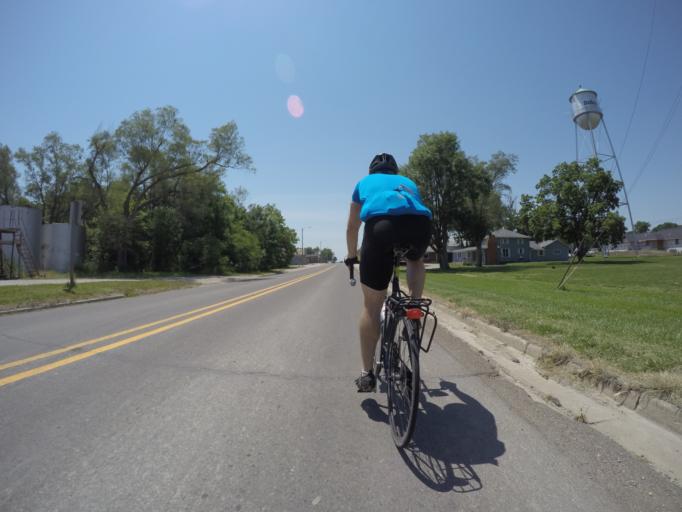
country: US
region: Nebraska
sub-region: Pawnee County
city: Pawnee City
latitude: 40.0356
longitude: -96.0482
